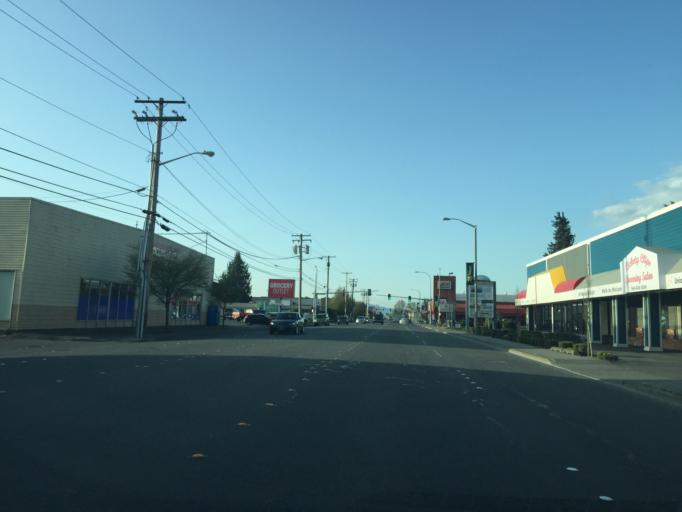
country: US
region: Washington
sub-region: Skagit County
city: Mount Vernon
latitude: 48.4324
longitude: -122.3352
